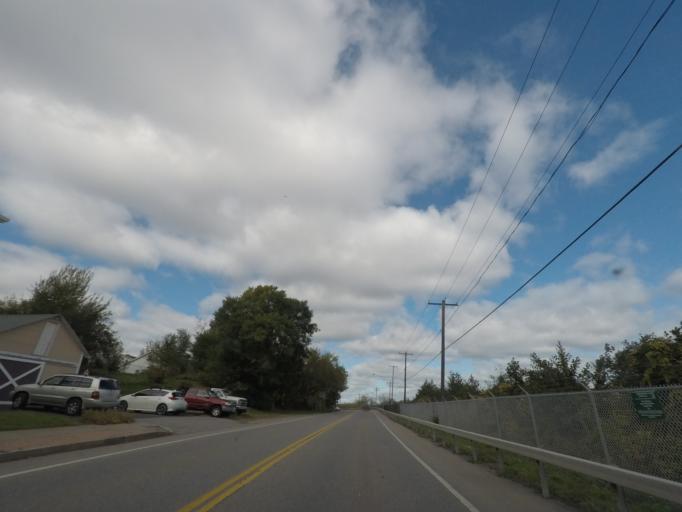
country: US
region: New York
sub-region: Albany County
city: Cohoes
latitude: 42.7904
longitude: -73.7125
